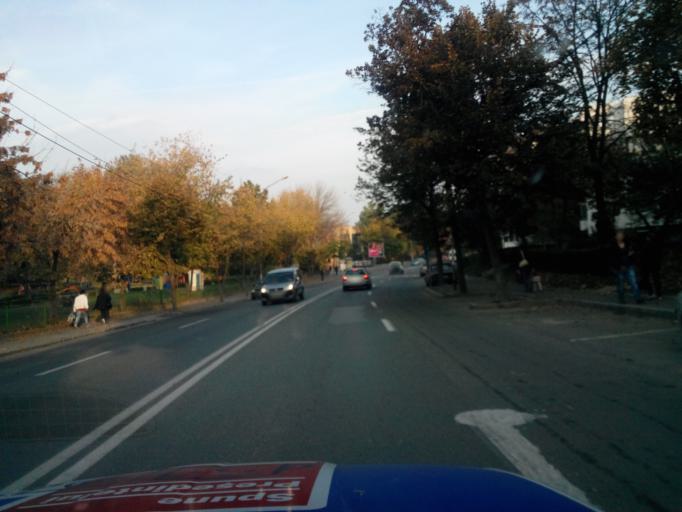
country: RO
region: Tulcea
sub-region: Municipiul Tulcea
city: Tulcea
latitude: 45.1803
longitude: 28.7796
